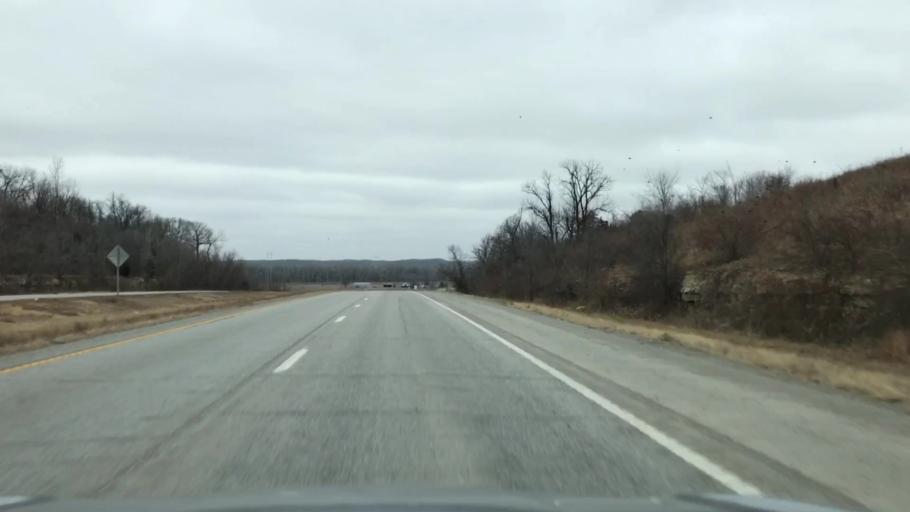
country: US
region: Missouri
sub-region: Jackson County
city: Independence
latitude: 39.1517
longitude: -94.3930
